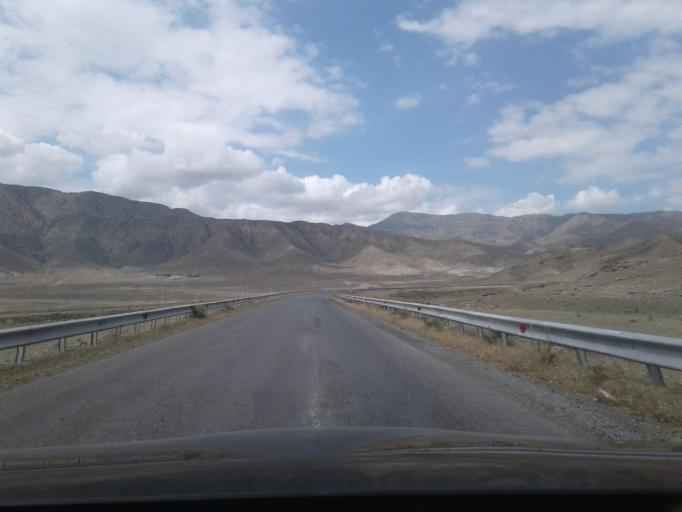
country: TM
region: Ahal
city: Baharly
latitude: 38.5037
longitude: 57.1237
